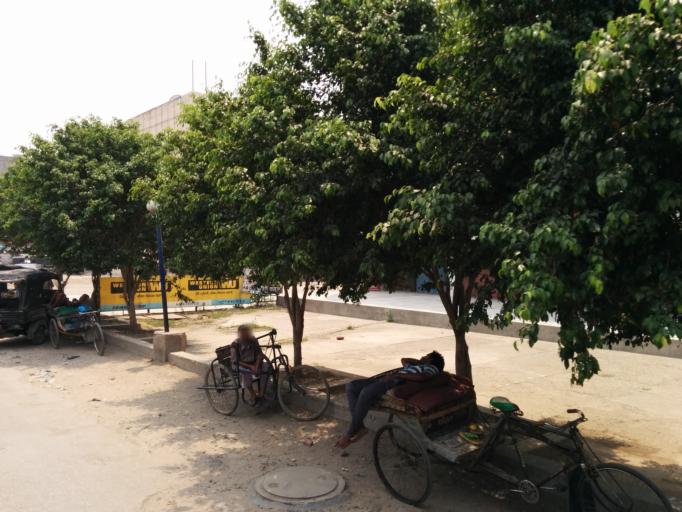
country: IN
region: Punjab
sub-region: Amritsar
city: Amritsar
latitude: 31.6280
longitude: 74.8841
